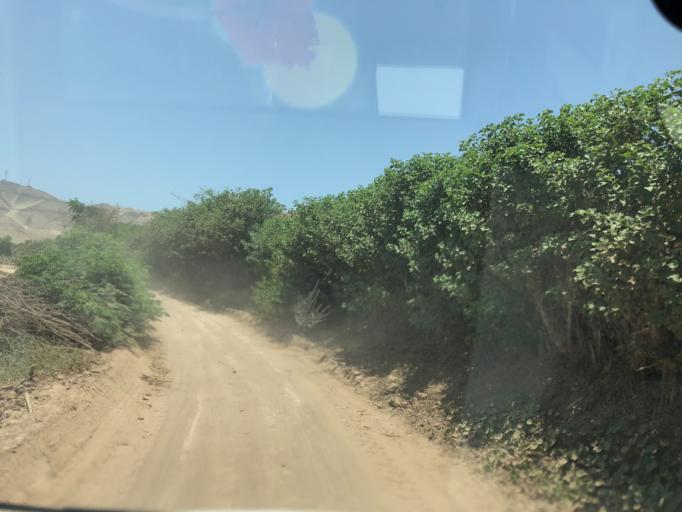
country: PE
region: Lima
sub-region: Provincia de Canete
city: Quilmana
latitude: -12.9971
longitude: -76.4419
